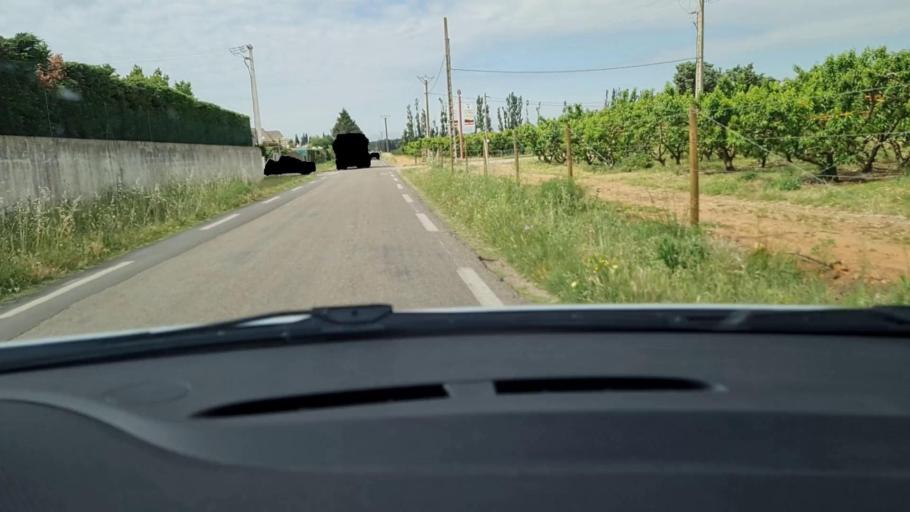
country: FR
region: Languedoc-Roussillon
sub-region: Departement du Gard
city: Jonquieres-Saint-Vincent
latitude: 43.8046
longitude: 4.5407
